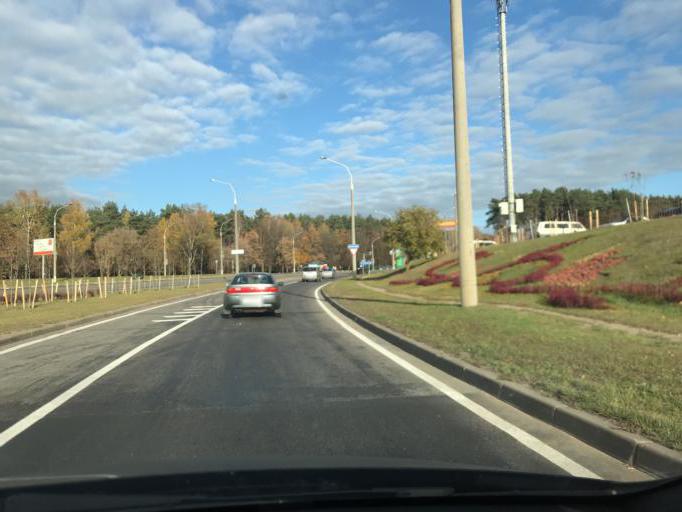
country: BY
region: Minsk
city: Borovlyany
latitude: 53.9605
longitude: 27.6310
